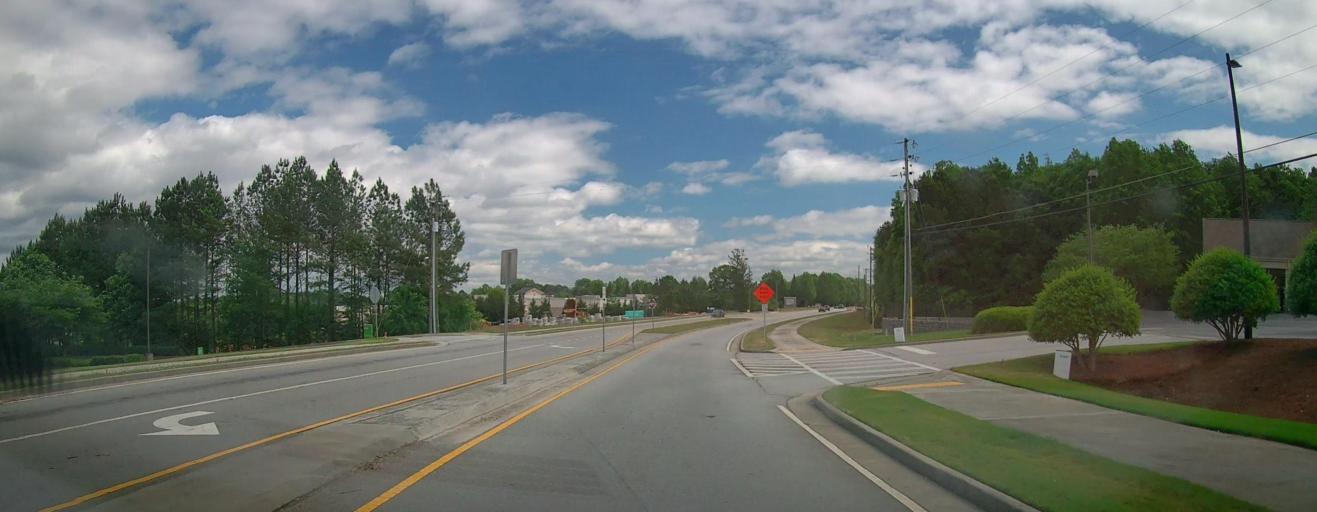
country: US
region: Georgia
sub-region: Rockdale County
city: Conyers
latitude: 33.6362
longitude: -84.0188
